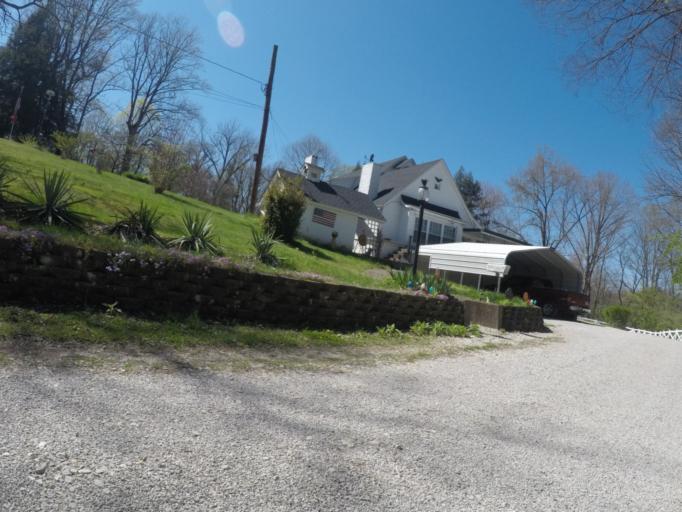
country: US
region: West Virginia
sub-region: Cabell County
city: Pea Ridge
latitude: 38.4188
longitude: -82.3194
